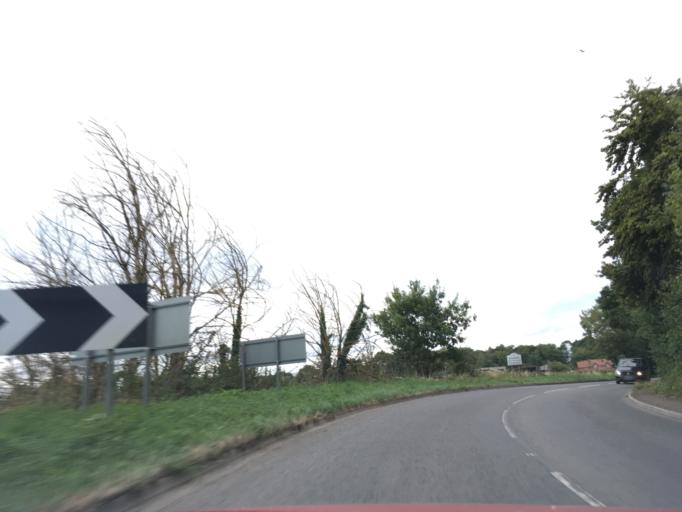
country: GB
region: England
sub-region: Wiltshire
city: Devizes
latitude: 51.3690
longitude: -2.0369
